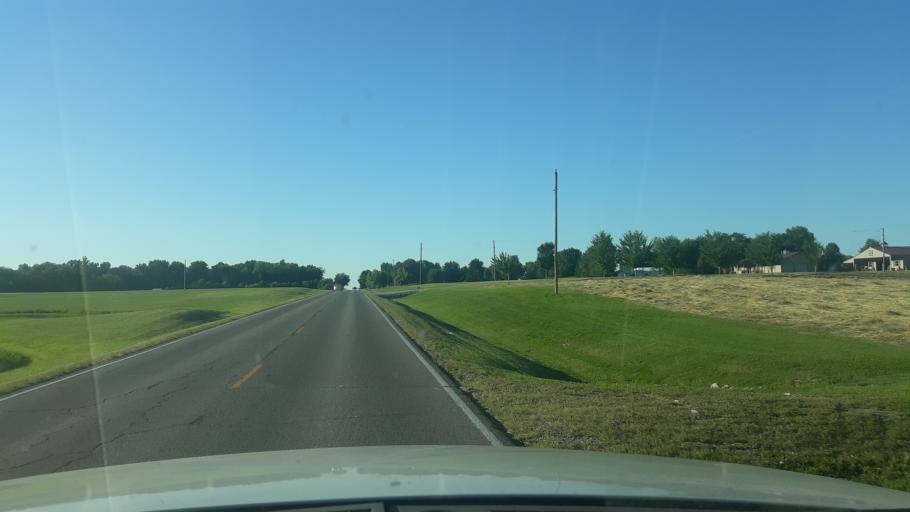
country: US
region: Illinois
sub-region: Saline County
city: Harrisburg
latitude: 37.8558
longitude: -88.6055
